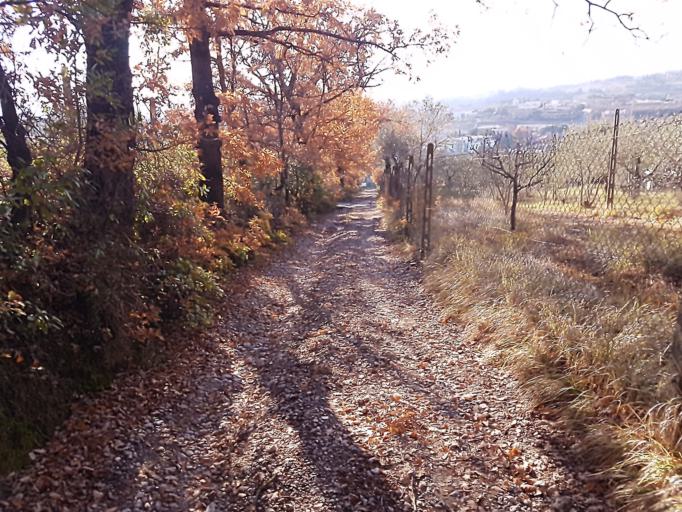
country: IT
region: Umbria
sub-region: Provincia di Perugia
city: Perugia
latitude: 43.0944
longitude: 12.3739
